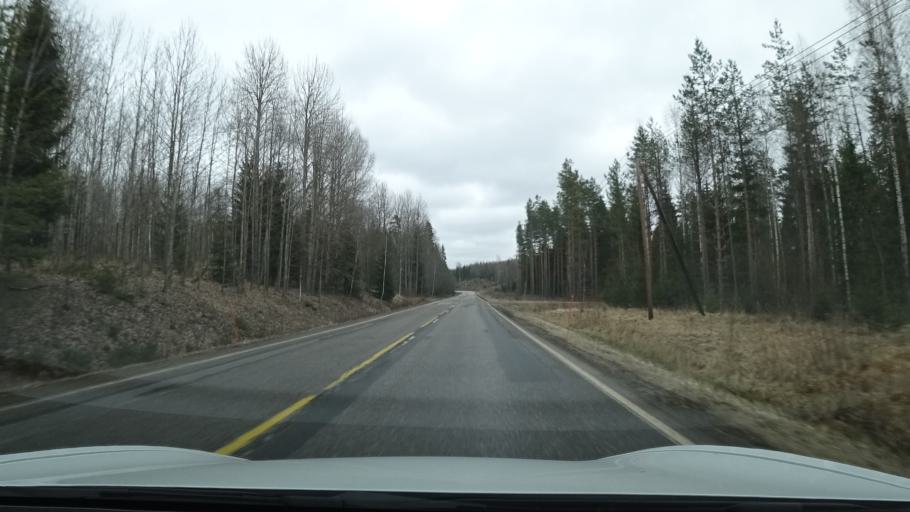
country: FI
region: Uusimaa
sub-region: Porvoo
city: Myrskylae
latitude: 60.6634
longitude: 25.7654
